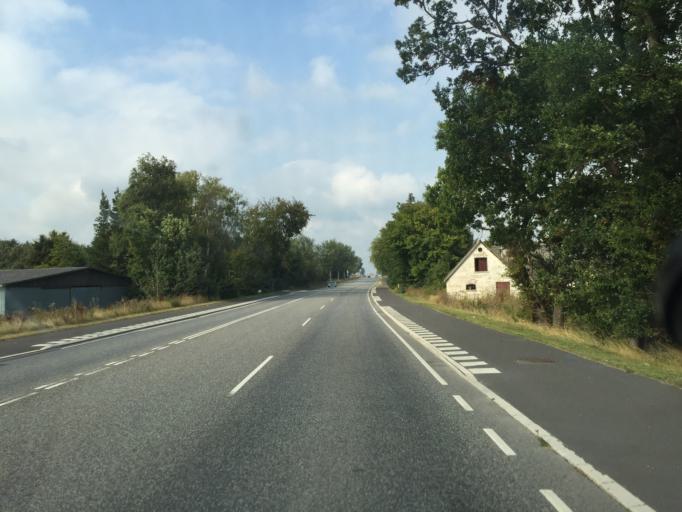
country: DK
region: Zealand
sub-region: Solrod Kommune
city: Havdrup
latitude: 55.5796
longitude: 12.1108
